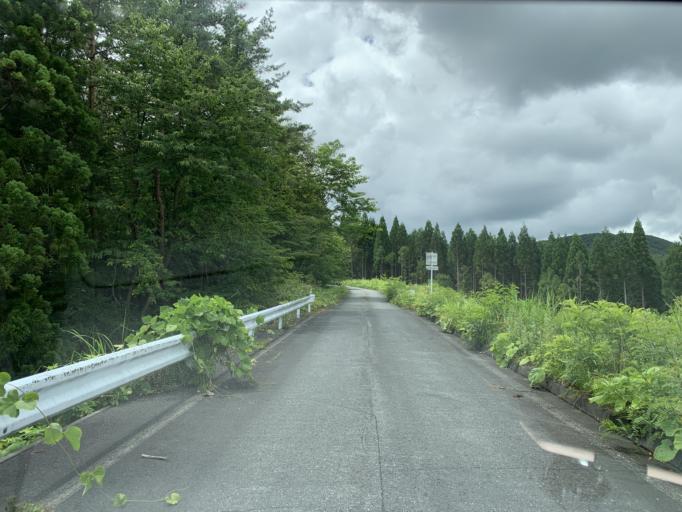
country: JP
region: Iwate
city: Ichinoseki
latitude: 38.9336
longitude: 140.9044
